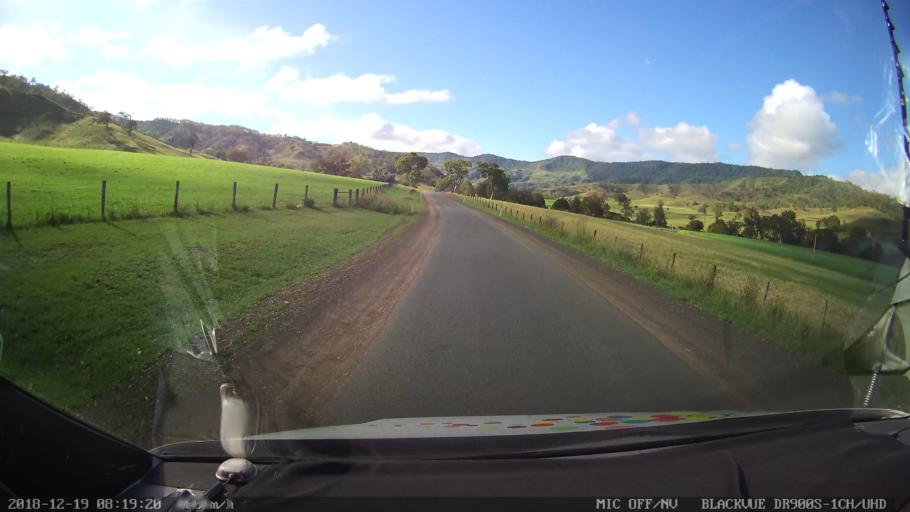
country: AU
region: New South Wales
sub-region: Kyogle
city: Kyogle
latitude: -28.2806
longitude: 152.9087
